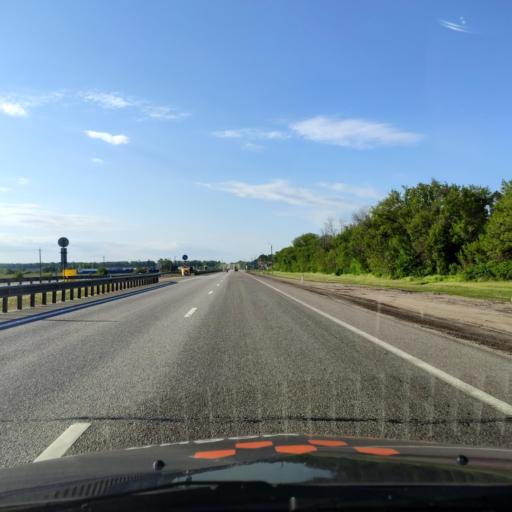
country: RU
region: Lipetsk
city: Khlevnoye
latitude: 52.0477
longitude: 39.1952
